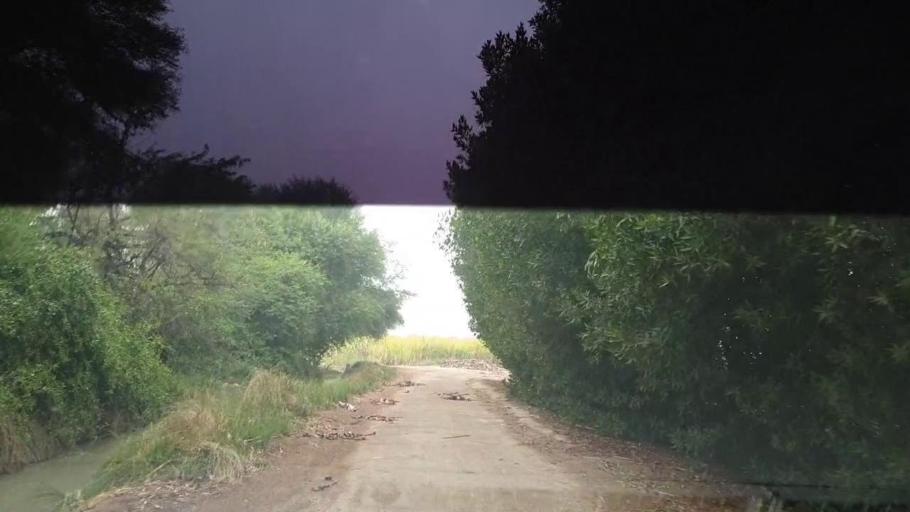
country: PK
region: Sindh
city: Tando Adam
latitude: 25.7762
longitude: 68.7306
